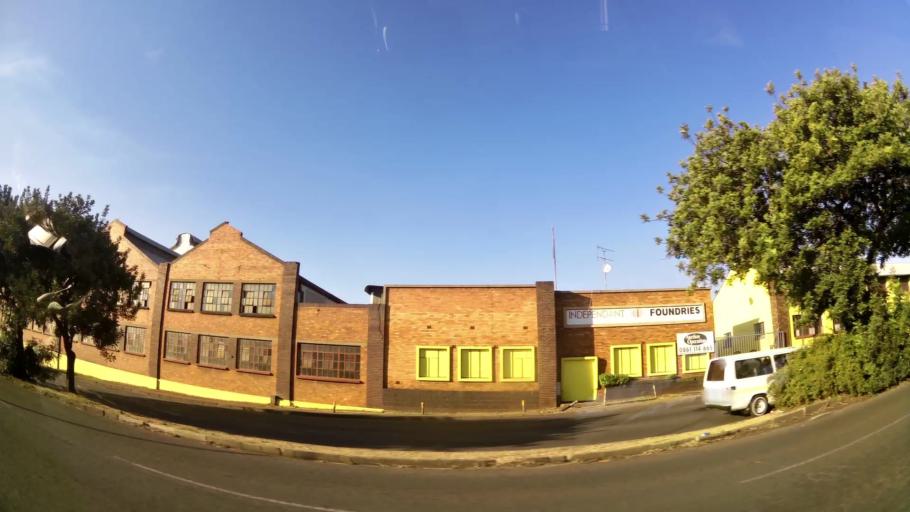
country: ZA
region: Gauteng
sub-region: City of Johannesburg Metropolitan Municipality
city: Roodepoort
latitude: -26.1522
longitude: 27.8650
